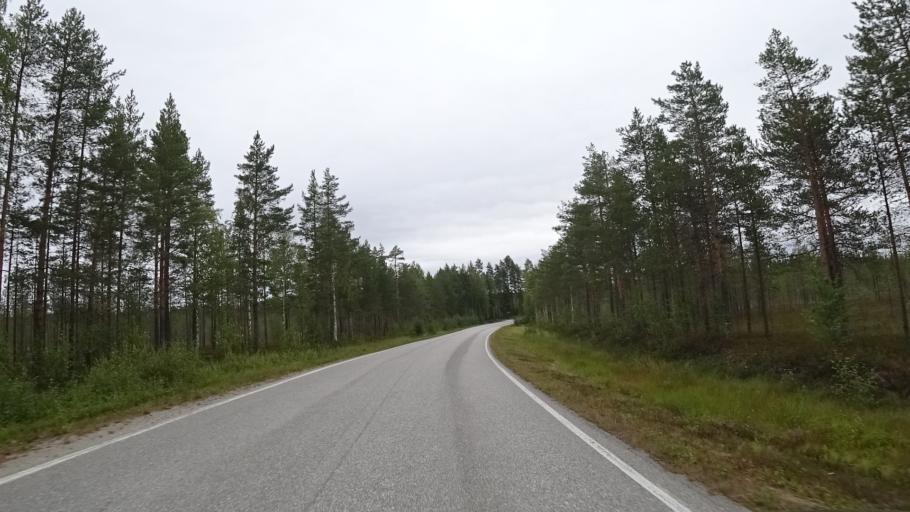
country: FI
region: North Karelia
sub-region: Pielisen Karjala
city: Lieksa
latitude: 63.3583
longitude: 30.2615
